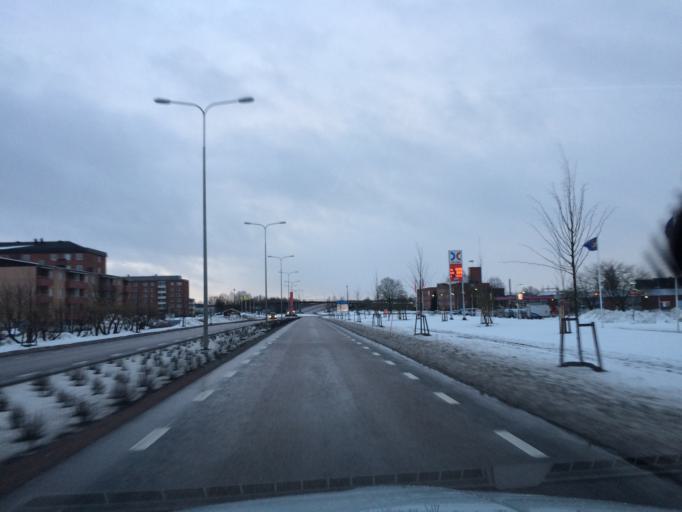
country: SE
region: Vaestmanland
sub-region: Kopings Kommun
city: Koping
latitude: 59.5120
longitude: 15.9851
